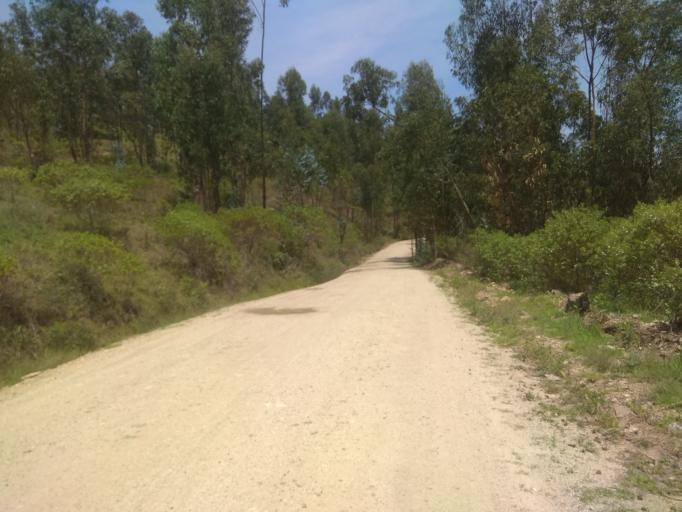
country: CO
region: Boyaca
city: Socha Viejo
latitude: 5.9799
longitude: -72.7313
